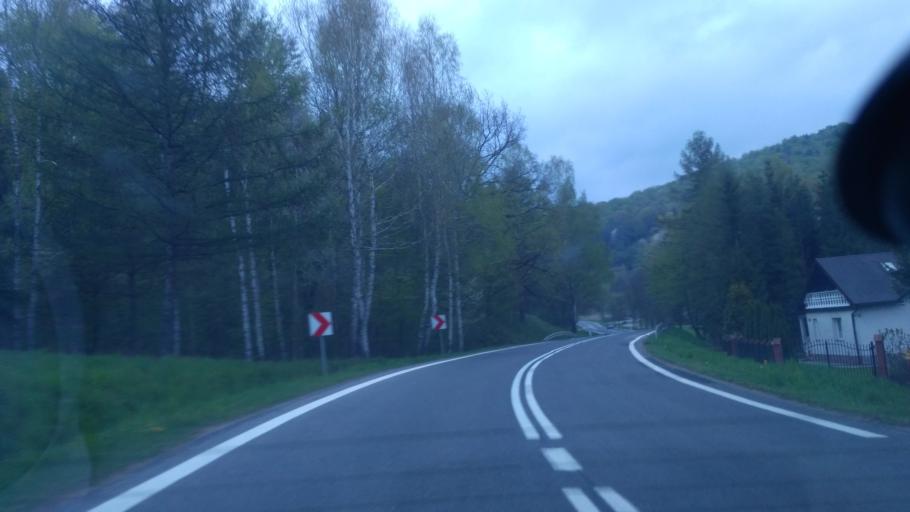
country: PL
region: Subcarpathian Voivodeship
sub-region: Powiat sanocki
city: Zagorz
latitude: 49.5351
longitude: 22.2994
